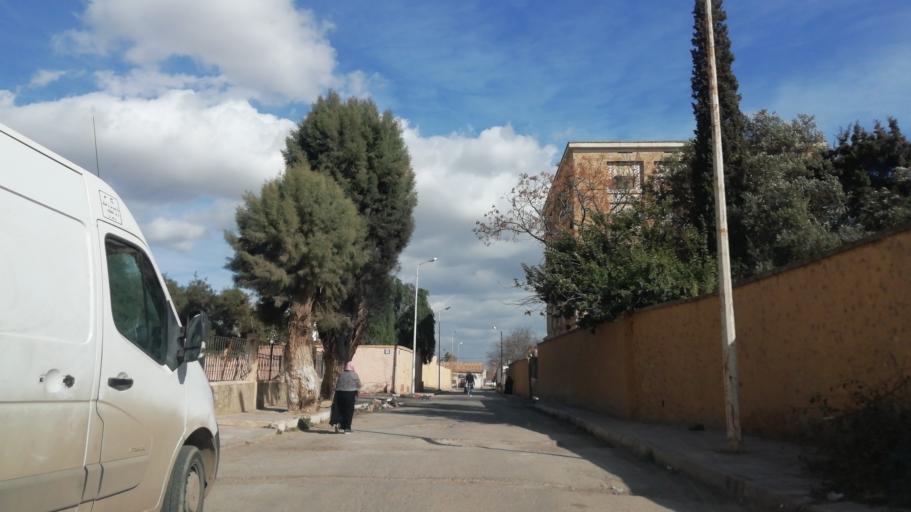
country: DZ
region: Oran
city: Es Senia
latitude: 35.6106
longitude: -0.5764
